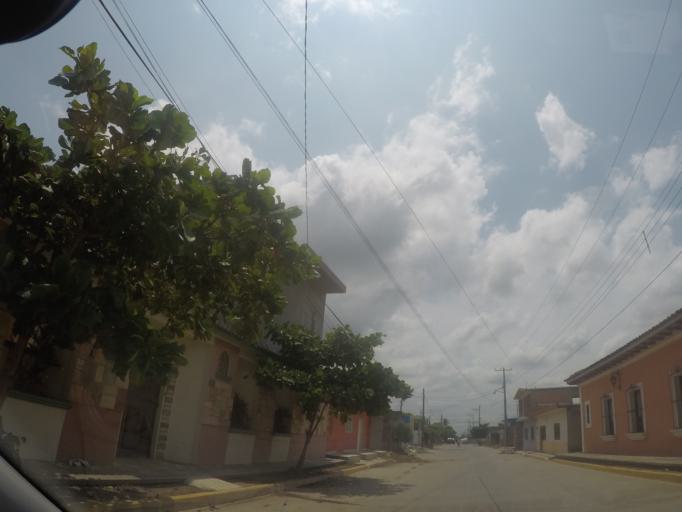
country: MX
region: Oaxaca
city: El Espinal
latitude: 16.5510
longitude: -94.9481
